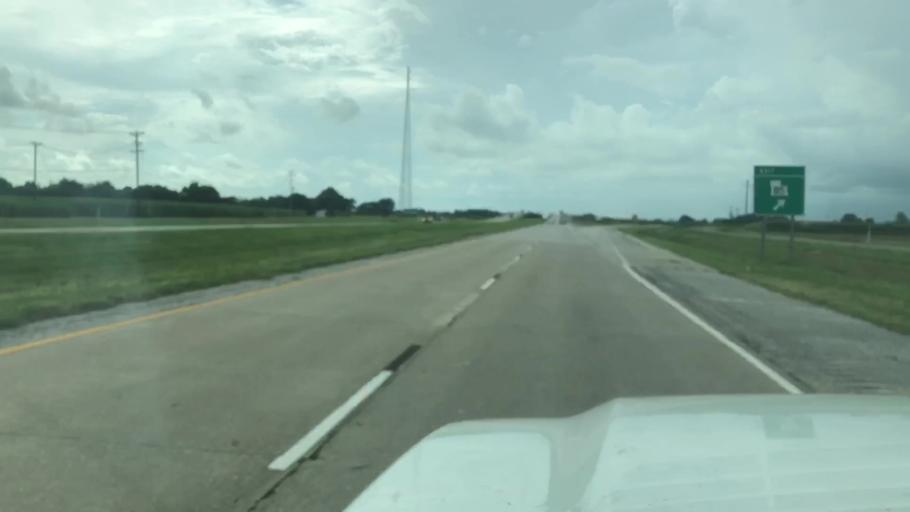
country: US
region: Louisiana
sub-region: Iberia Parish
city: Jeanerette
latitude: 29.9160
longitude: -91.7227
